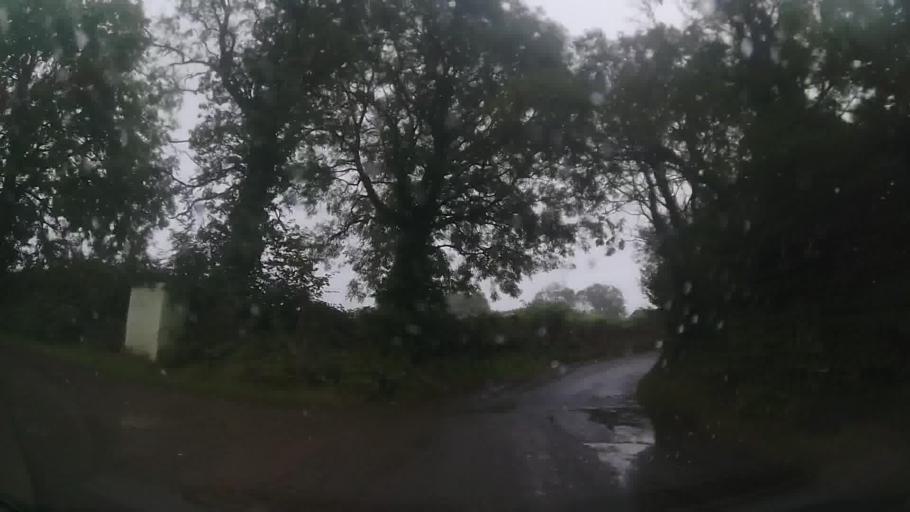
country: GB
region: Wales
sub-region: Carmarthenshire
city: Whitland
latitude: 51.7601
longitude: -4.6360
